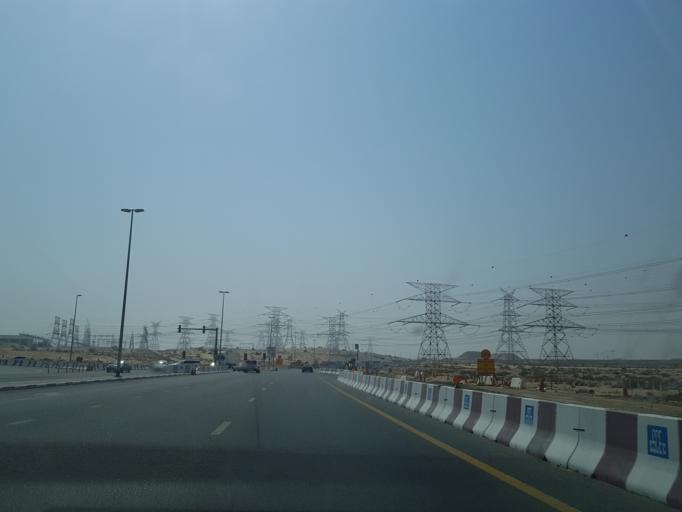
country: AE
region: Ash Shariqah
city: Sharjah
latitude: 25.1496
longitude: 55.4162
